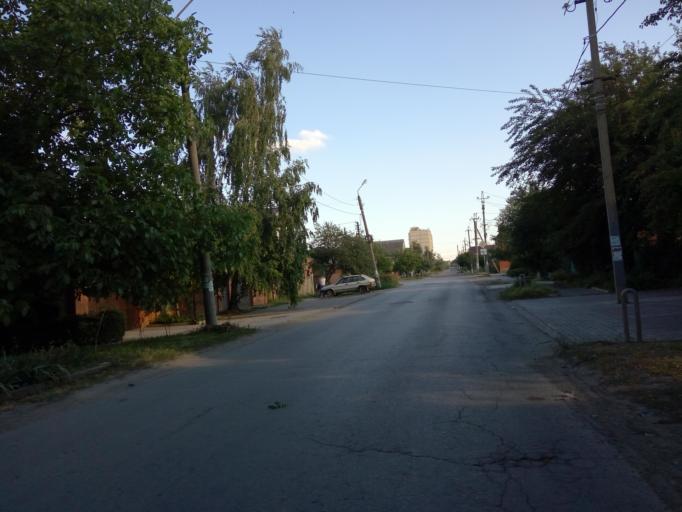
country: RU
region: Rostov
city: Bataysk
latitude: 47.1217
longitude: 39.7356
